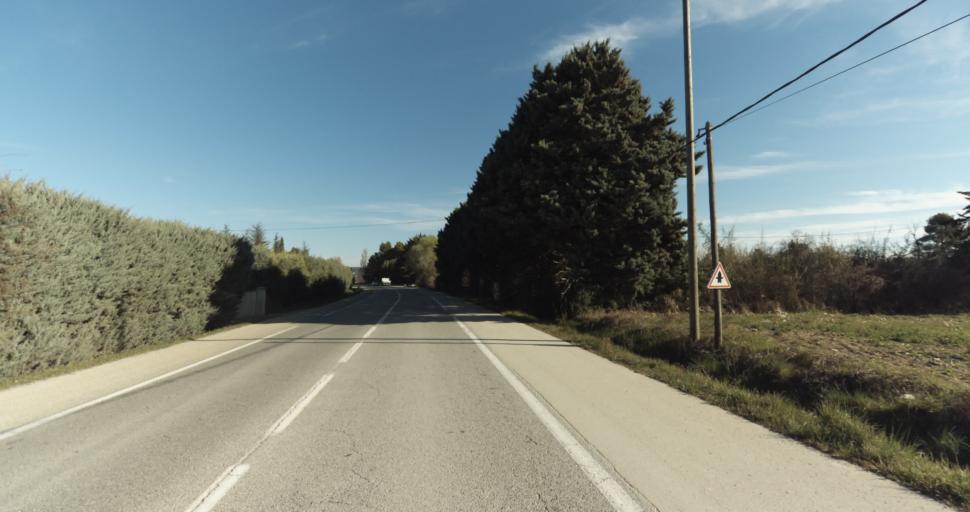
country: FR
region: Provence-Alpes-Cote d'Azur
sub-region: Departement des Bouches-du-Rhone
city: Aix-en-Provence
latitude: 43.5645
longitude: 5.4342
